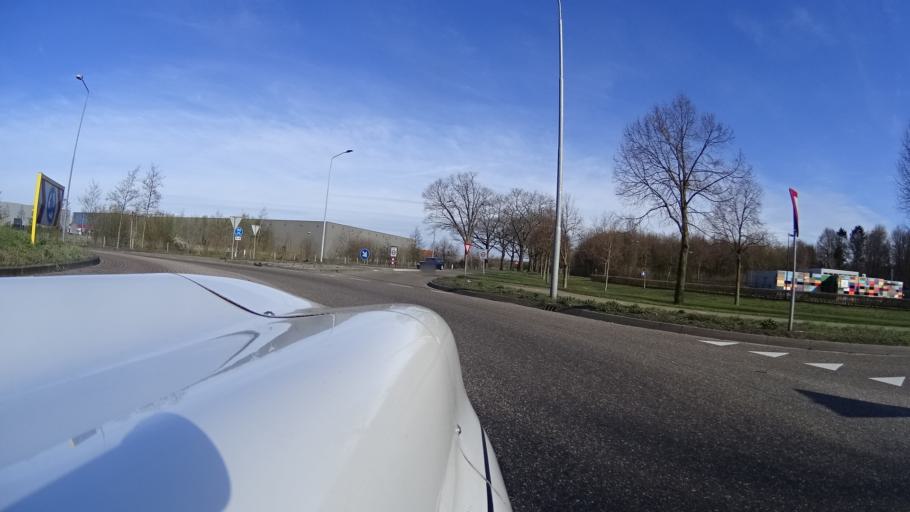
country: NL
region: North Brabant
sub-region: Gemeente Uden
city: Volkel
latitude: 51.6553
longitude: 5.6733
